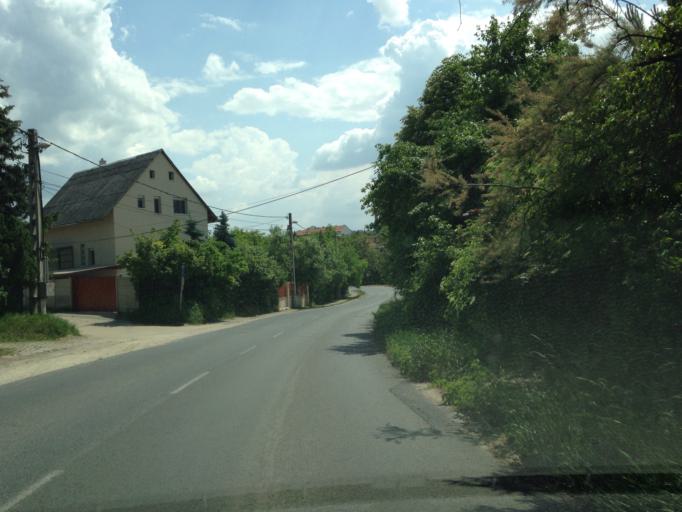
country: HU
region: Pest
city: Szentendre
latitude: 47.6822
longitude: 19.0625
